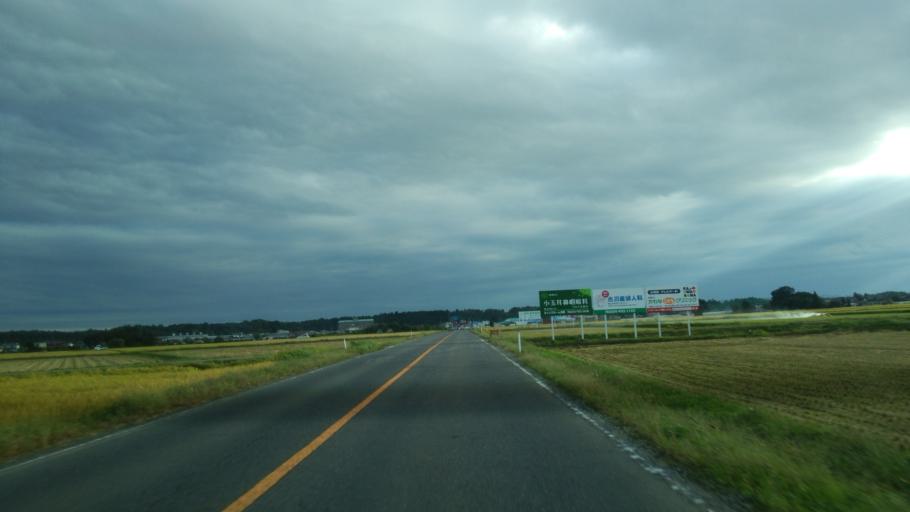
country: JP
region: Fukushima
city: Koriyama
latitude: 37.3709
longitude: 140.3407
